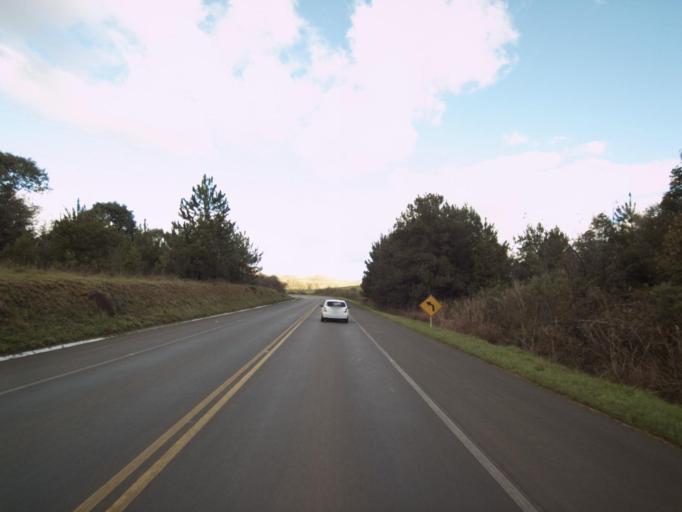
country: BR
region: Santa Catarina
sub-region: Campos Novos
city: Campos Novos
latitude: -27.3261
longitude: -51.3599
